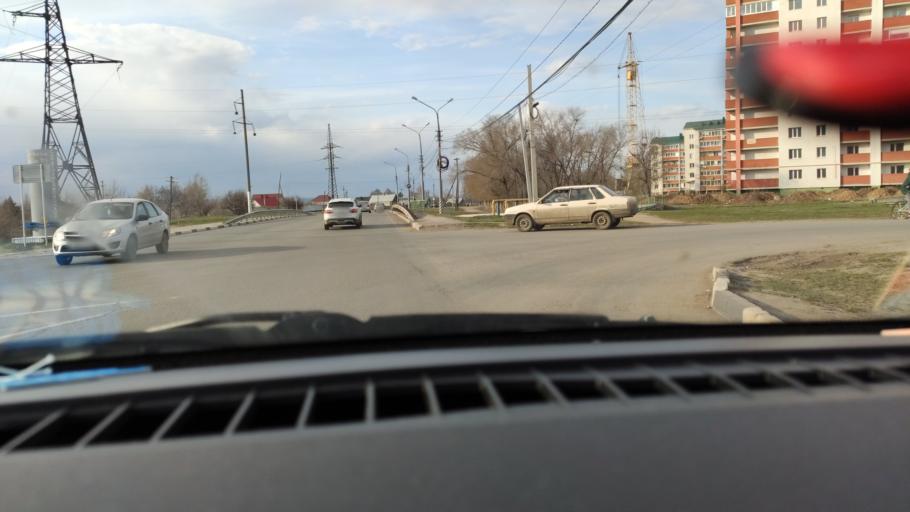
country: RU
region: Saratov
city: Privolzhskiy
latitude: 51.3980
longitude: 46.0347
